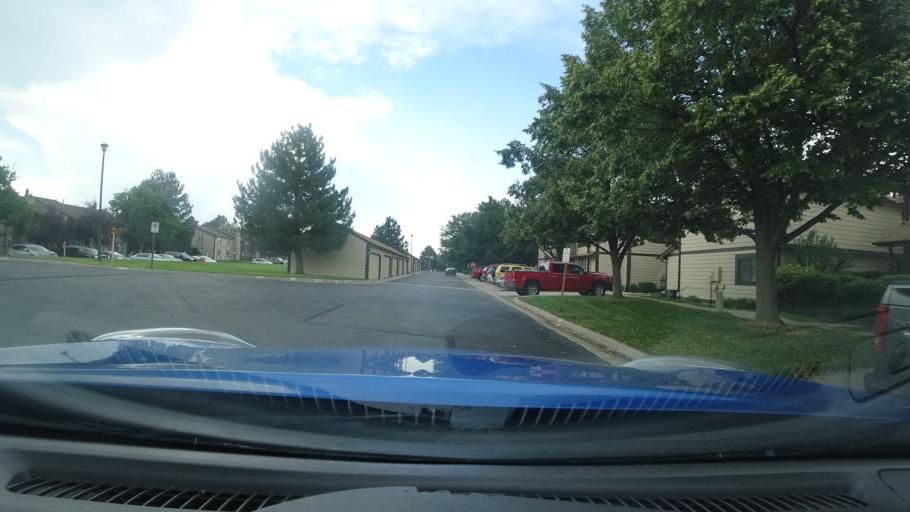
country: US
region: Colorado
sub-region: Adams County
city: Aurora
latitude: 39.6834
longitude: -104.7859
